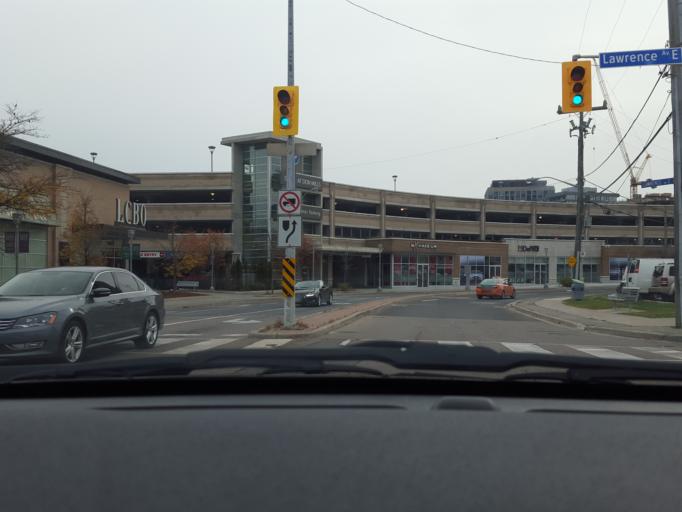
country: CA
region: Ontario
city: Willowdale
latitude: 43.7365
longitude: -79.3466
